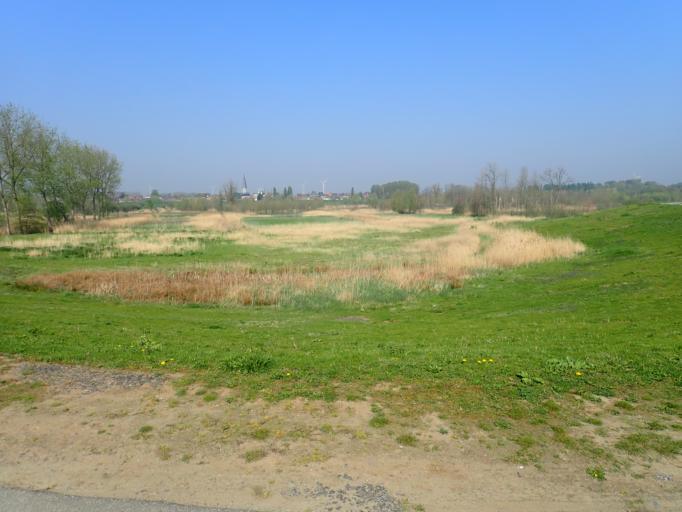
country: BE
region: Flanders
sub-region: Provincie Oost-Vlaanderen
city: Kruibeke
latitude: 51.1676
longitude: 4.3257
